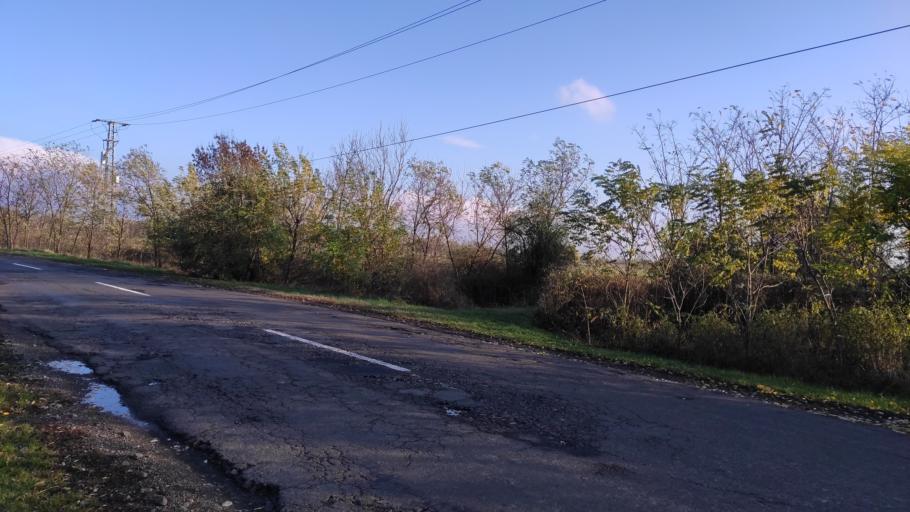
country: HU
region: Bekes
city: Mezobereny
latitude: 46.7609
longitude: 21.0507
